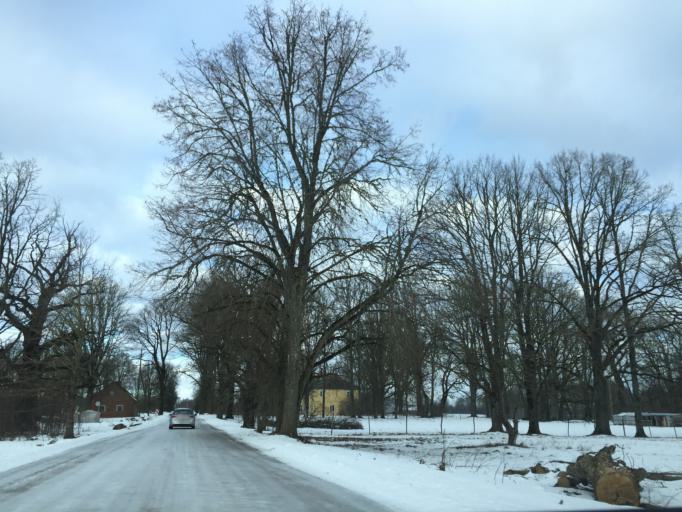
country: LV
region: Lielvarde
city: Lielvarde
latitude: 56.5640
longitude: 24.7344
